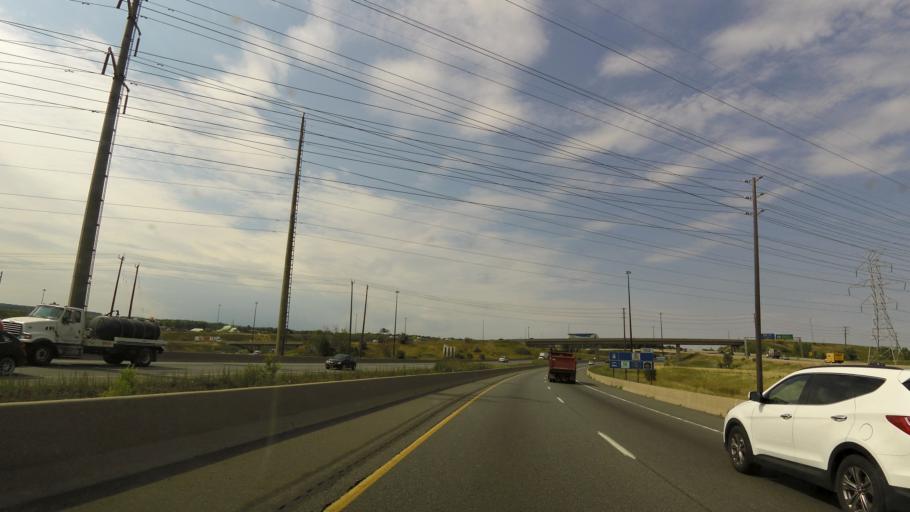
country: CA
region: Ontario
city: Burlington
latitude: 43.3334
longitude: -79.8288
